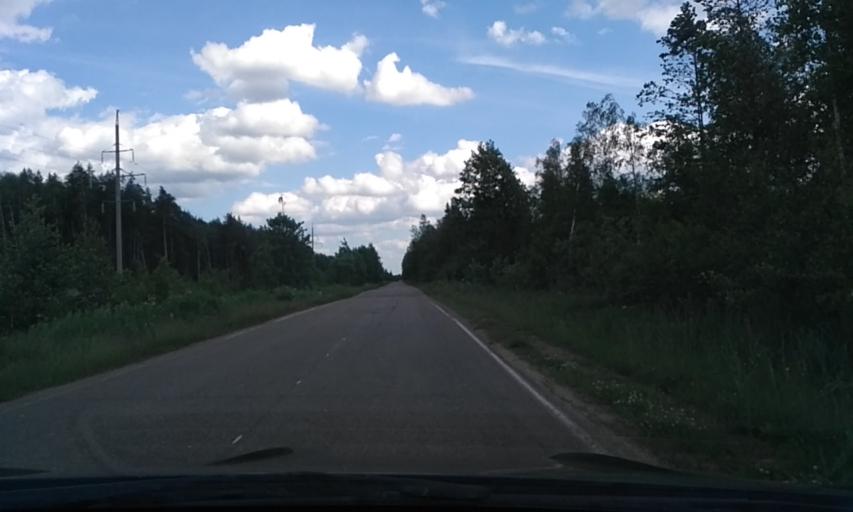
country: RU
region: Leningrad
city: Otradnoye
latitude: 59.8205
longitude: 30.7964
